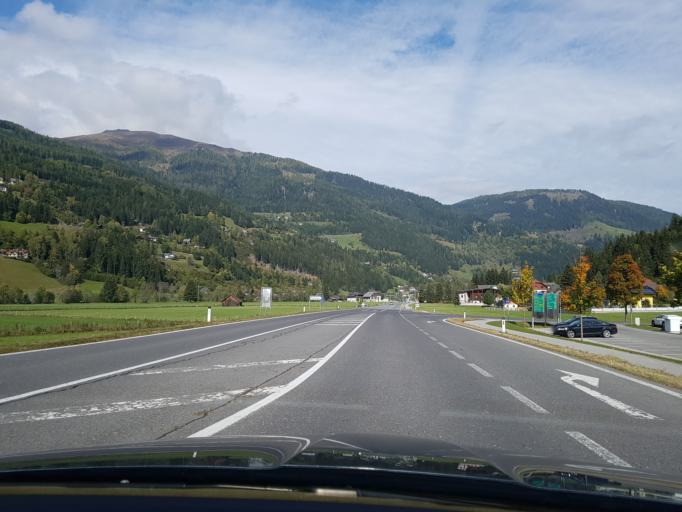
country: AT
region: Carinthia
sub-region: Politischer Bezirk Spittal an der Drau
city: Kleinkirchheim
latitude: 46.8177
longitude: 13.8634
